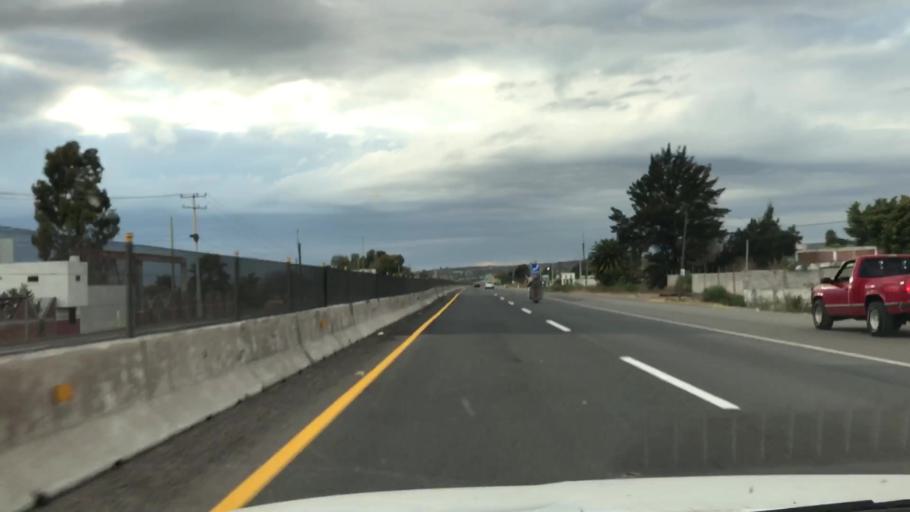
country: MX
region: Guanajuato
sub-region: Penjamo
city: Estacion la Piedad
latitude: 20.3884
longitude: -101.9402
